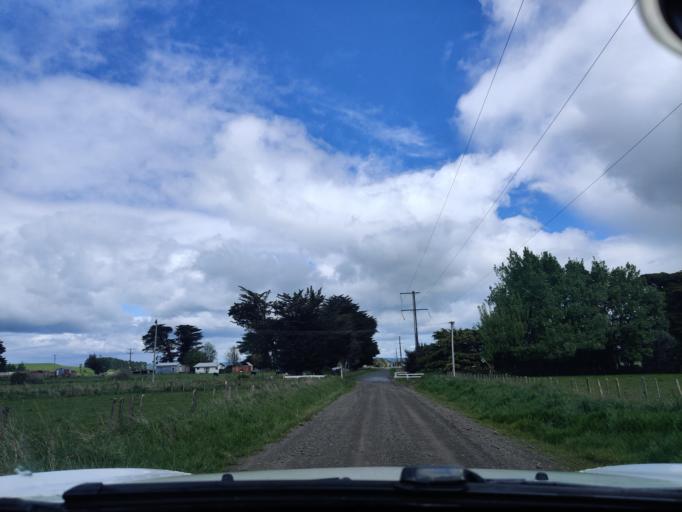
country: NZ
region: Manawatu-Wanganui
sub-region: Palmerston North City
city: Palmerston North
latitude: -40.3060
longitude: 175.8602
